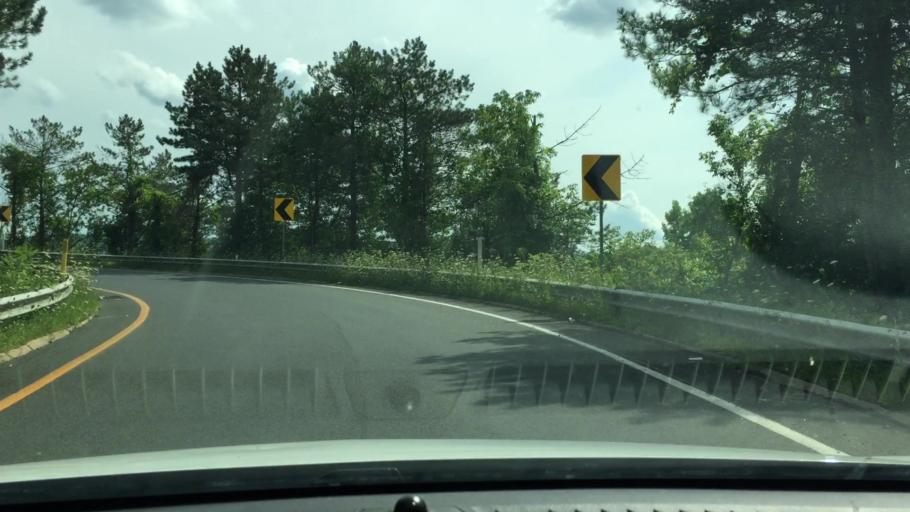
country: US
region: Massachusetts
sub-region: Berkshire County
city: Lee
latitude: 42.2971
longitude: -73.2402
